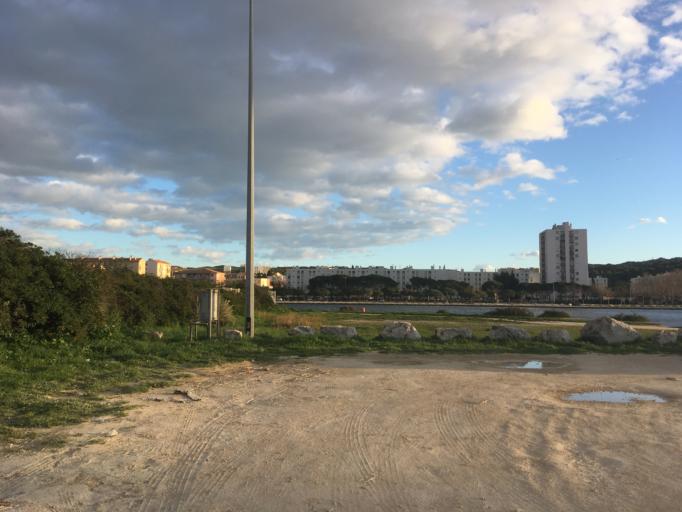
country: FR
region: Provence-Alpes-Cote d'Azur
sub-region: Departement des Bouches-du-Rhone
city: Martigues
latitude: 43.4041
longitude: 5.0457
